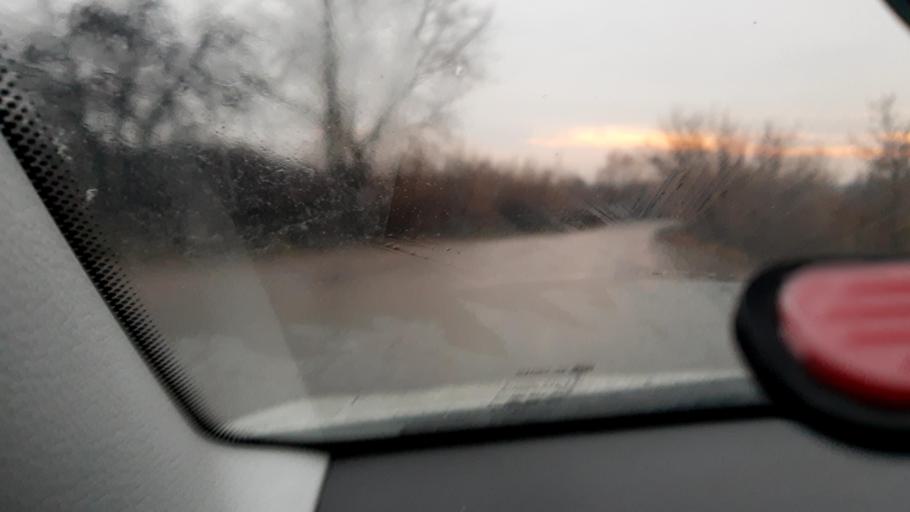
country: RU
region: Bashkortostan
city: Ufa
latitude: 54.8701
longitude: 56.1330
